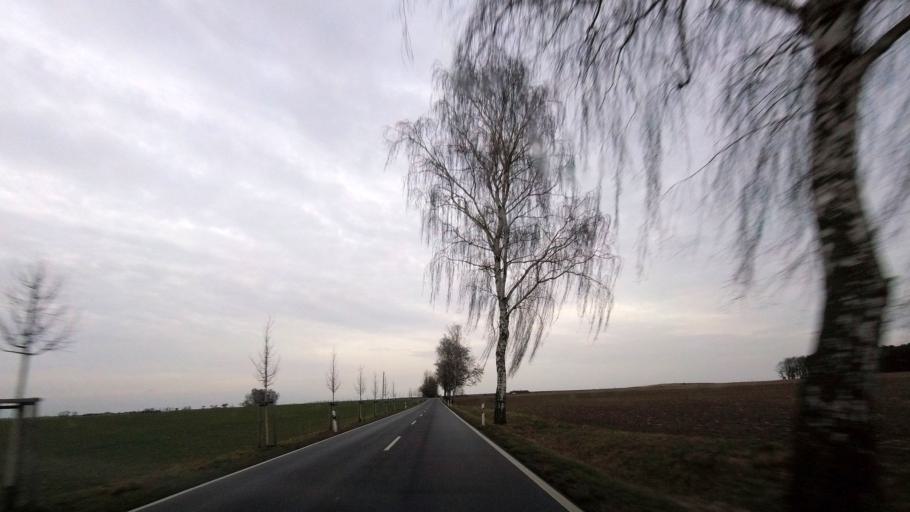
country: DE
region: Brandenburg
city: Niedergorsdorf
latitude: 51.9360
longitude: 12.9745
